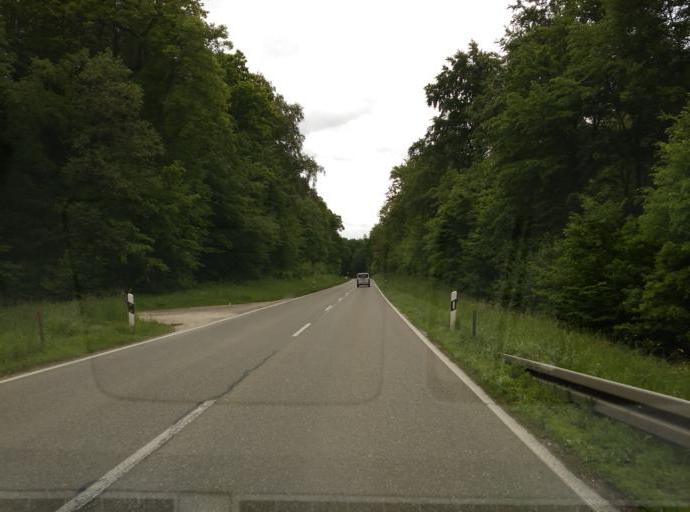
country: DE
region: Baden-Wuerttemberg
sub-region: Regierungsbezirk Stuttgart
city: Altdorf
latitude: 48.5853
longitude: 9.2870
